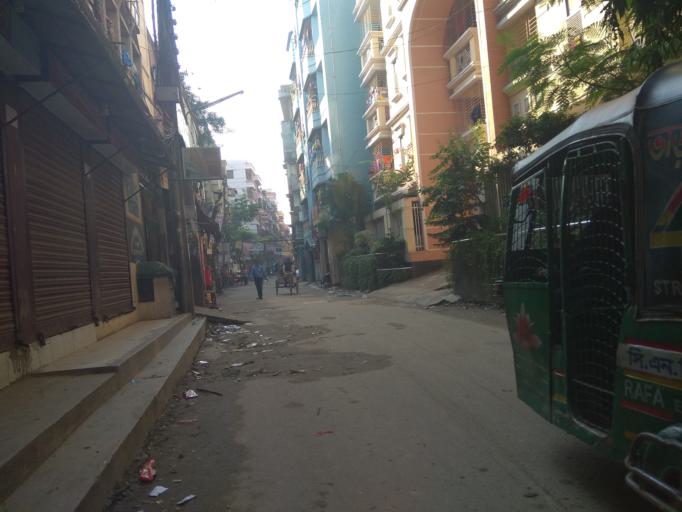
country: BD
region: Dhaka
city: Azimpur
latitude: 23.7609
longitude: 90.3574
